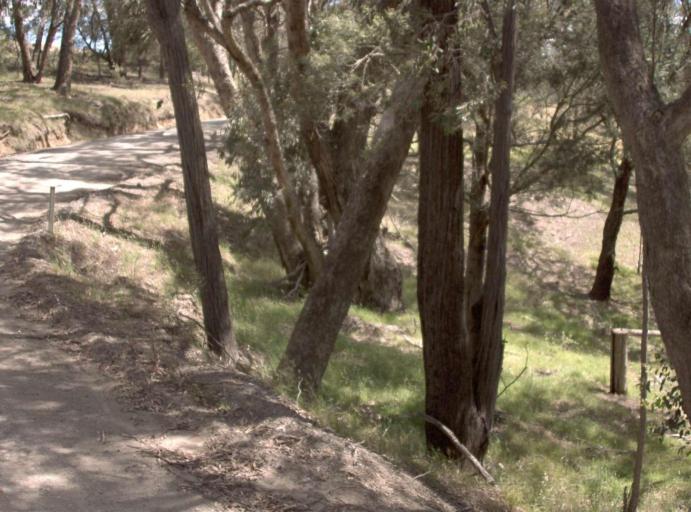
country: AU
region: New South Wales
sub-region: Bombala
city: Bombala
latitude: -37.1455
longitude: 148.6625
